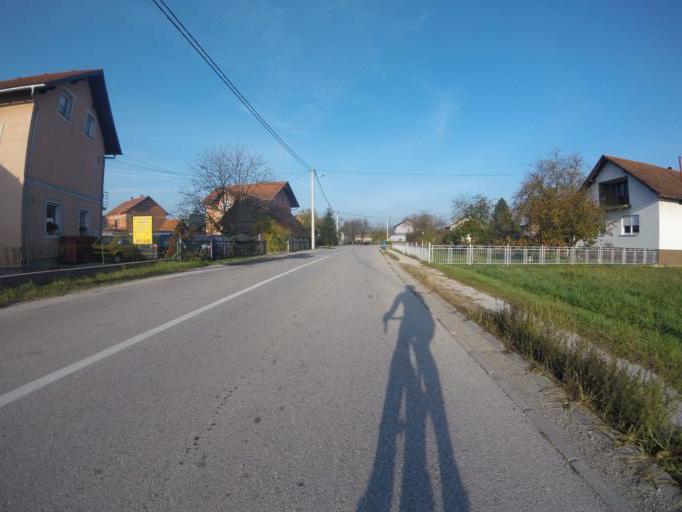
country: HR
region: Zagrebacka
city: Micevec
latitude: 45.7500
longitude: 16.0978
